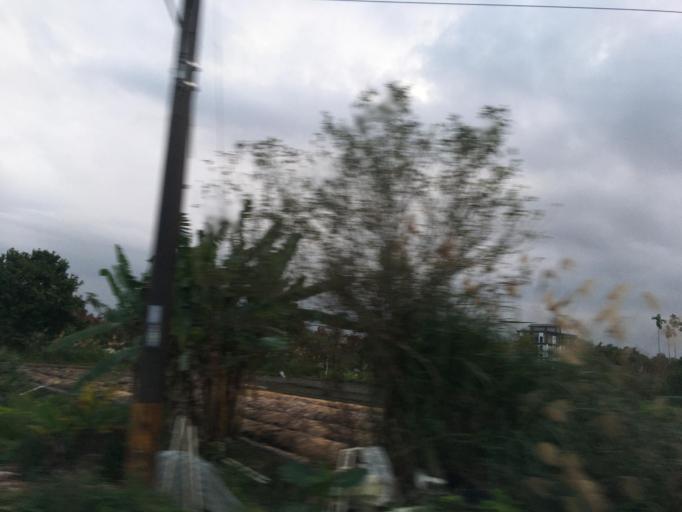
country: TW
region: Taiwan
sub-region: Yilan
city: Yilan
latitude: 24.7508
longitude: 121.7296
